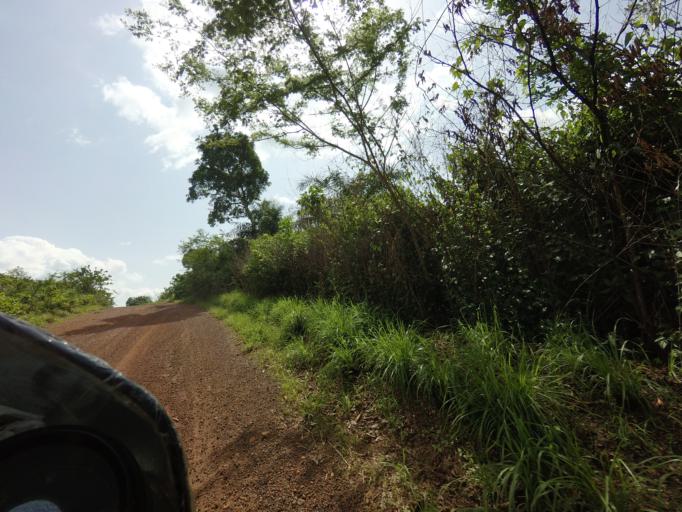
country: SL
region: Eastern Province
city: Daru
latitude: 8.0457
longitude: -10.8487
